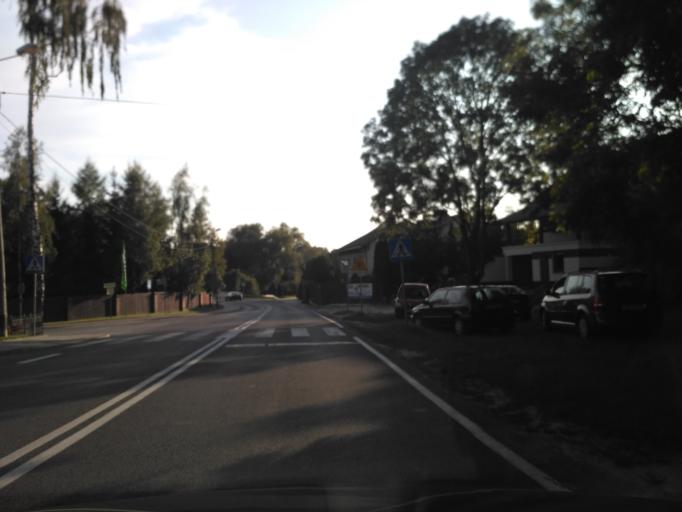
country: PL
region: Lublin Voivodeship
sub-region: Powiat lubelski
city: Bychawa
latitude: 51.0196
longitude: 22.5341
